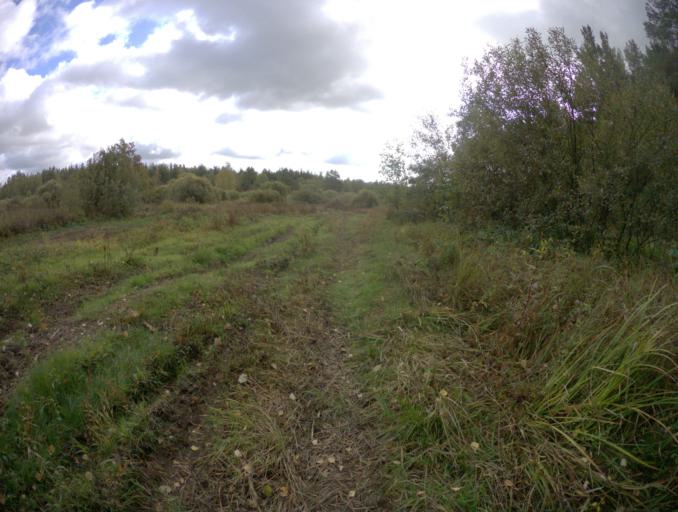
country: RU
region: Moskovskaya
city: Baksheyevo
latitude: 55.7141
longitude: 39.8523
